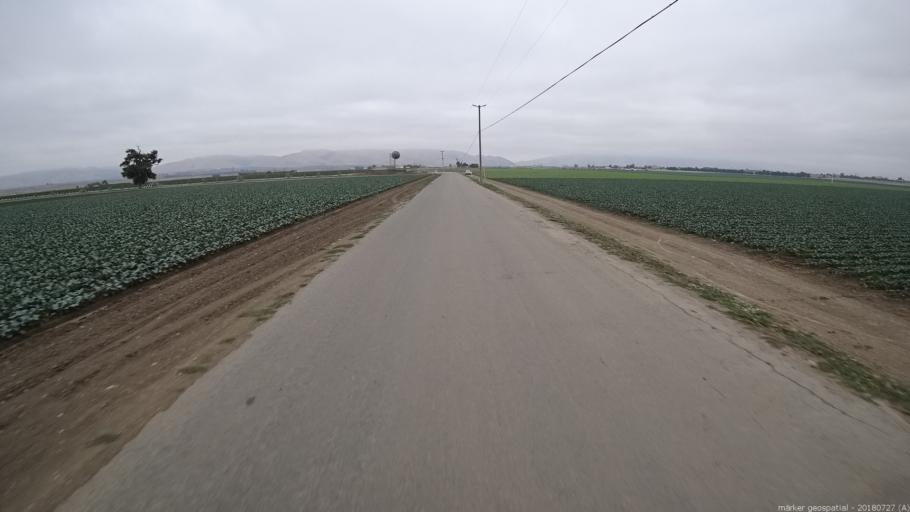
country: US
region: California
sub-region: Monterey County
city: Greenfield
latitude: 36.3148
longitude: -121.2184
